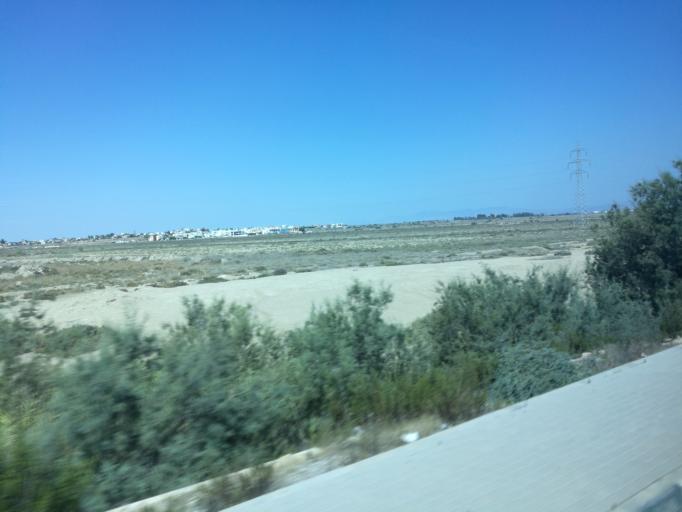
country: CY
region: Ammochostos
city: Famagusta
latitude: 35.1656
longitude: 33.8993
